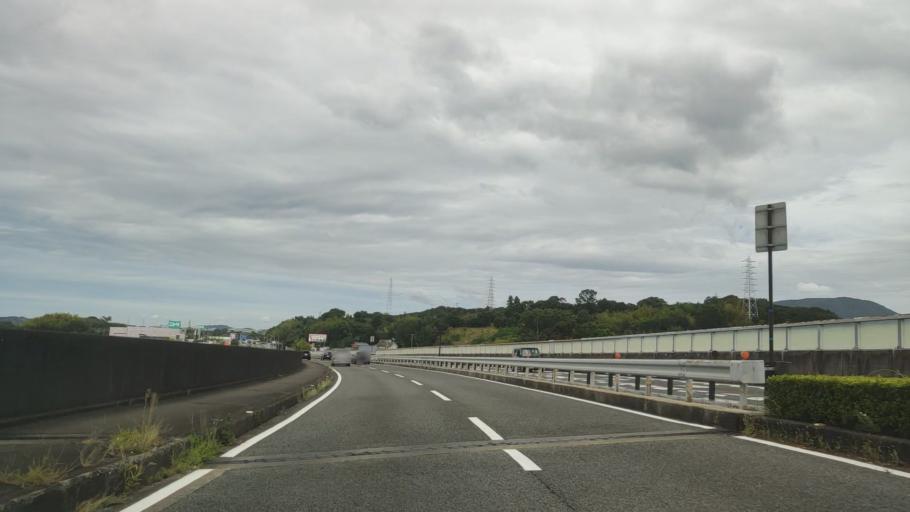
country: JP
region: Wakayama
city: Tanabe
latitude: 33.7173
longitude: 135.4078
